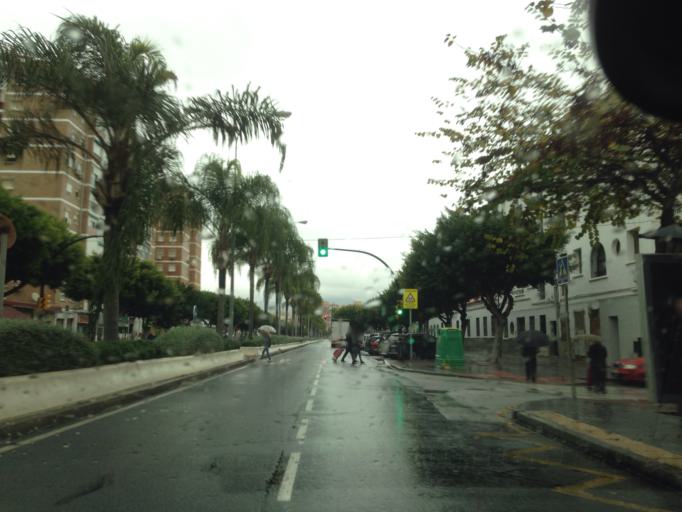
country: ES
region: Andalusia
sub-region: Provincia de Malaga
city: Malaga
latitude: 36.6959
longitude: -4.4425
